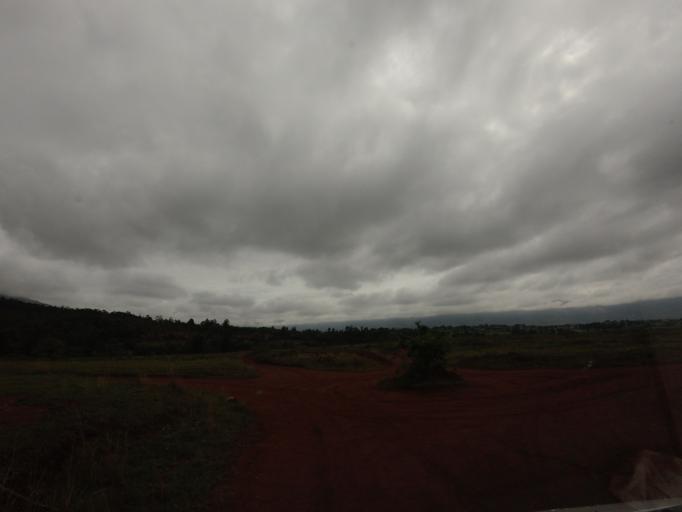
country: SZ
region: Hhohho
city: Lobamba
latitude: -26.4643
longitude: 31.1836
